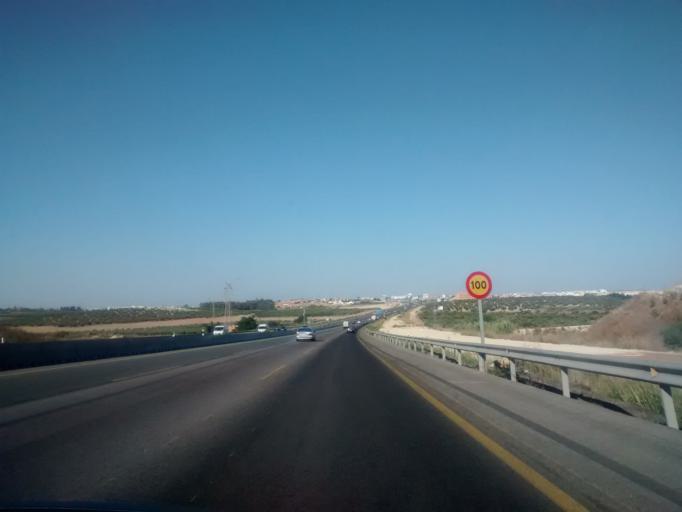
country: ES
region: Andalusia
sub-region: Provincia de Sevilla
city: Espartinas
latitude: 37.3695
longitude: -6.1023
